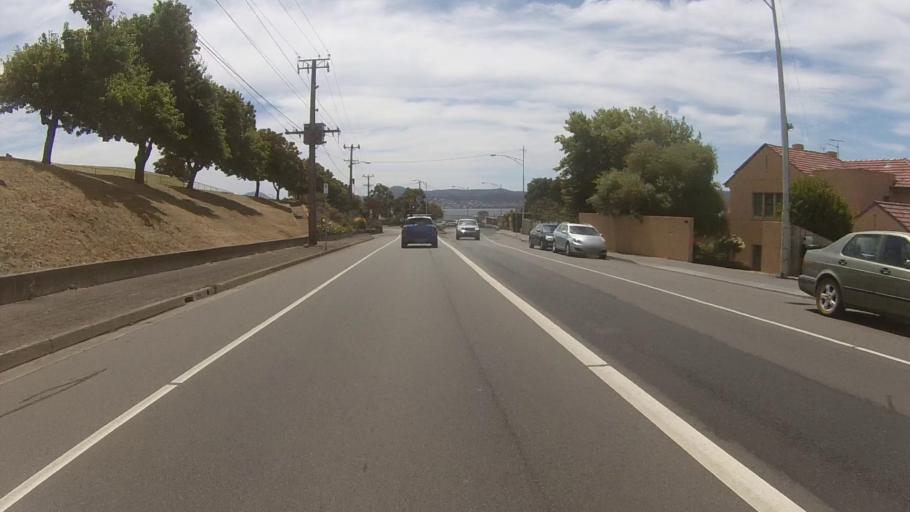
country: AU
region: Tasmania
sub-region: Kingborough
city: Taroona
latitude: -42.9158
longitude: 147.3588
